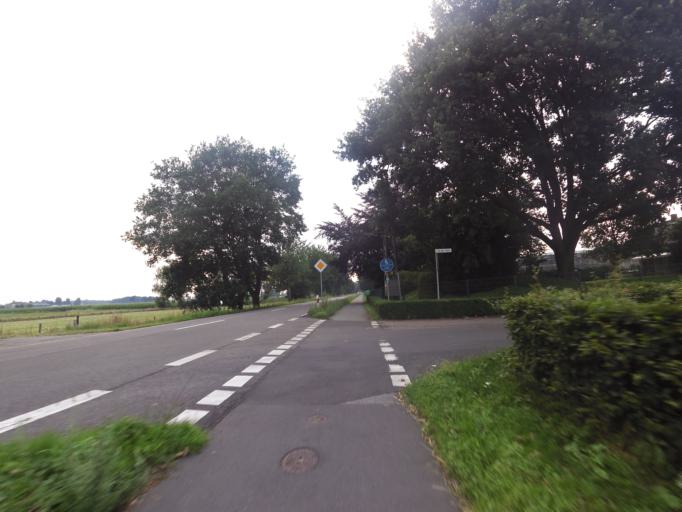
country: NL
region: Gelderland
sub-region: Oude IJsselstreek
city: Gendringen
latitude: 51.8569
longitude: 6.4051
